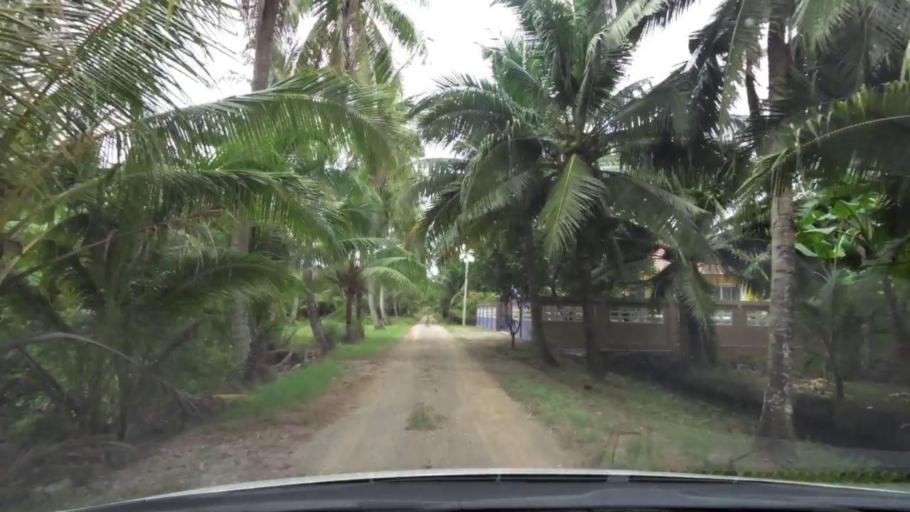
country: TH
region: Samut Sakhon
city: Ban Phaeo
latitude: 13.6116
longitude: 100.0287
